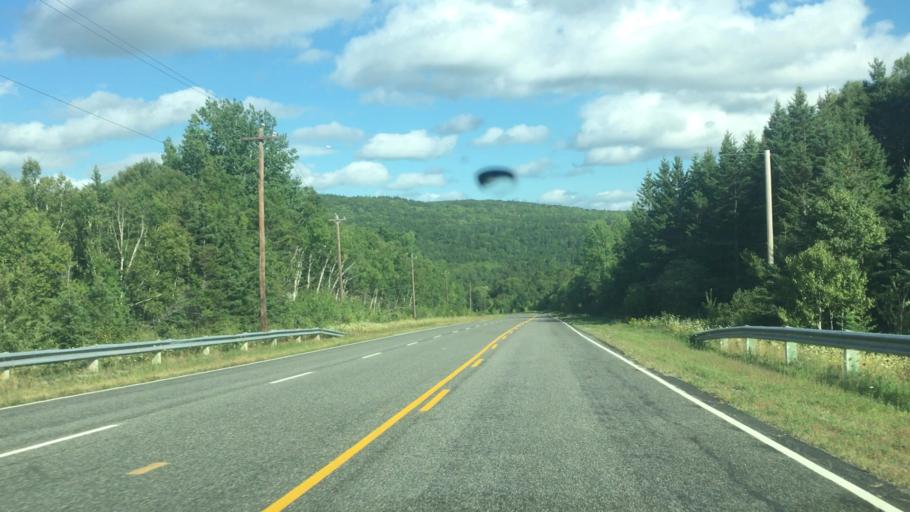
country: CA
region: Nova Scotia
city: Sydney
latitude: 45.8138
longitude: -60.6792
